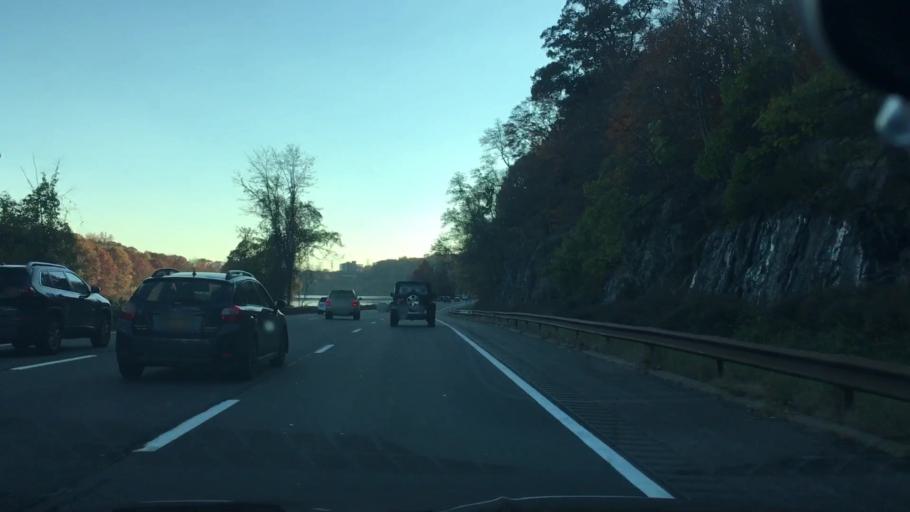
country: US
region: New York
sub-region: Westchester County
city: Greenville
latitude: 40.9812
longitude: -73.8470
